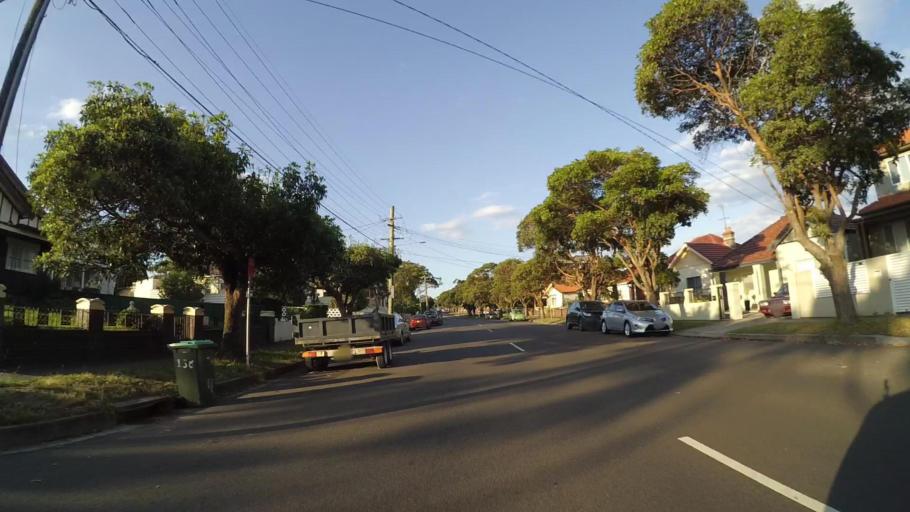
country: AU
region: New South Wales
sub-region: Randwick
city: Daceyville
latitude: -33.9295
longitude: 151.2324
